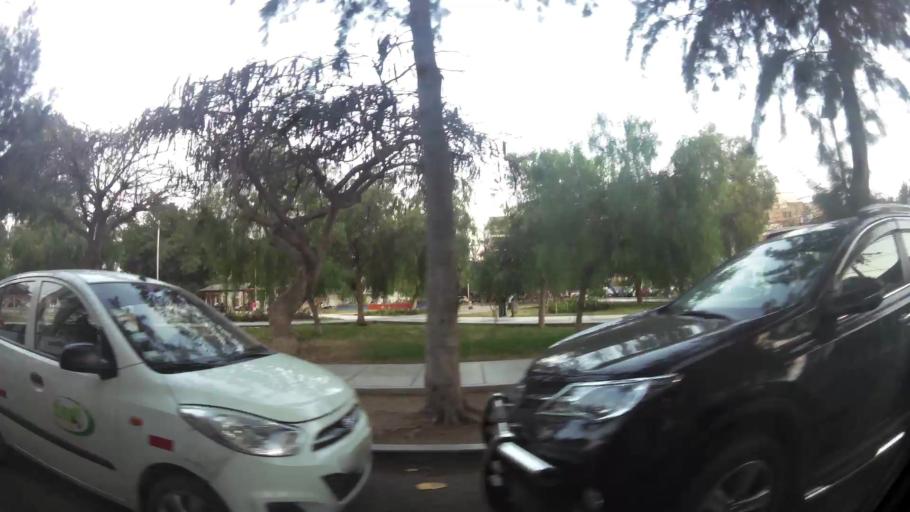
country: PE
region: La Libertad
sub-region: Provincia de Trujillo
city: Trujillo
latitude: -8.1029
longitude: -79.0371
